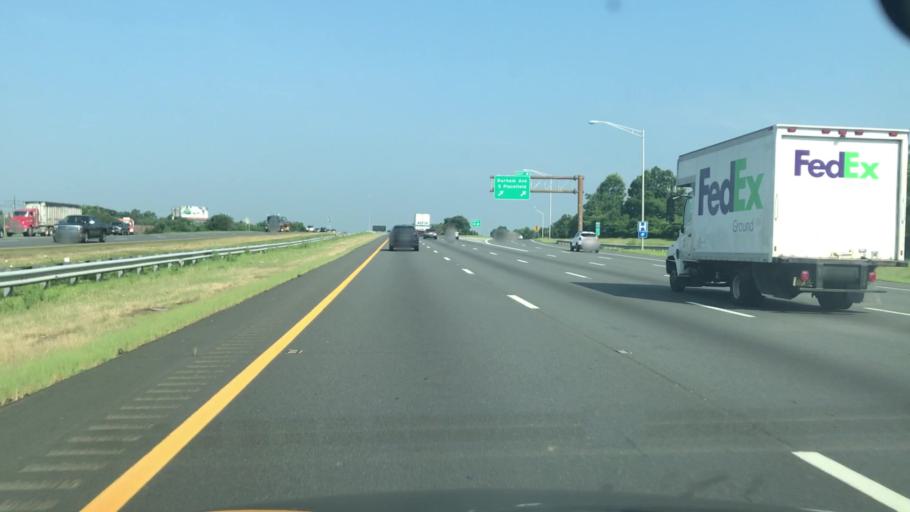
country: US
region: New Jersey
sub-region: Middlesex County
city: South Plainfield
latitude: 40.5512
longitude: -74.4092
